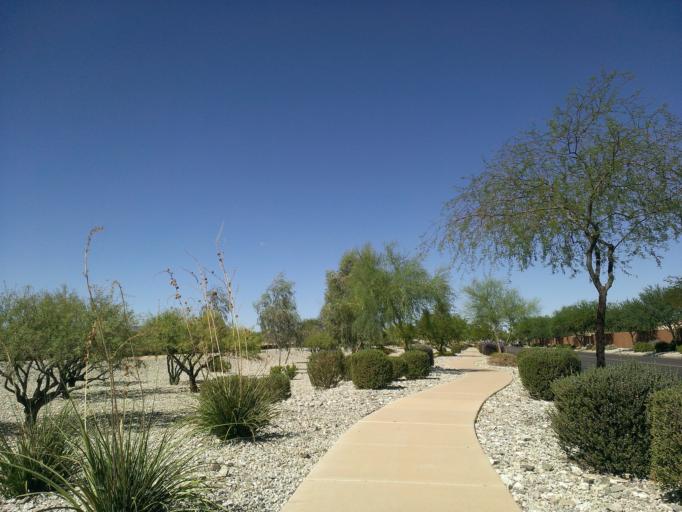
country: US
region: Arizona
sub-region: Pinal County
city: Arizona City
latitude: 32.8105
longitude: -111.6435
